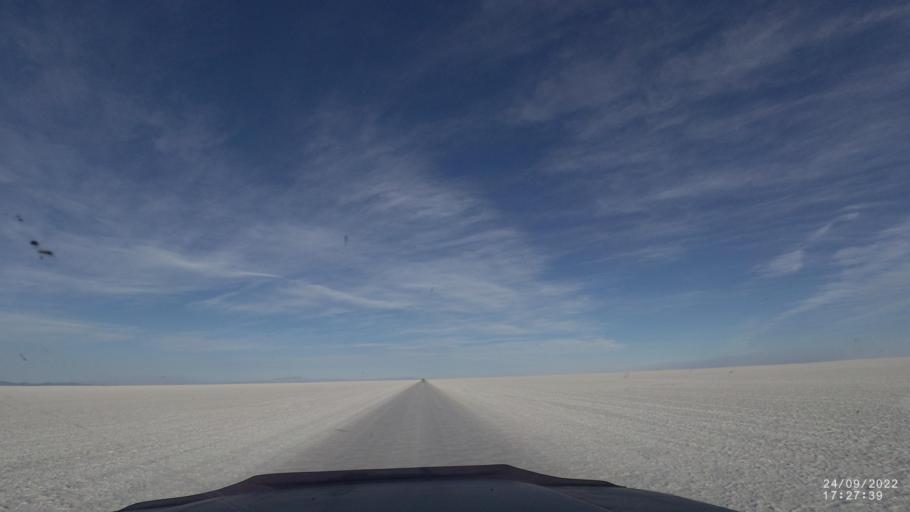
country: BO
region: Potosi
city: Colchani
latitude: -20.3006
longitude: -67.4439
